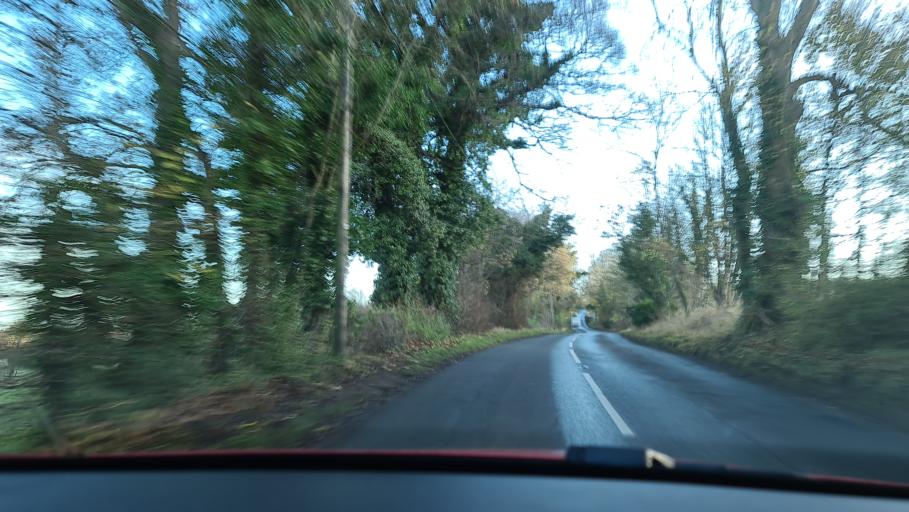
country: GB
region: England
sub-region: Buckinghamshire
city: Princes Risborough
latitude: 51.7517
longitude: -0.7947
